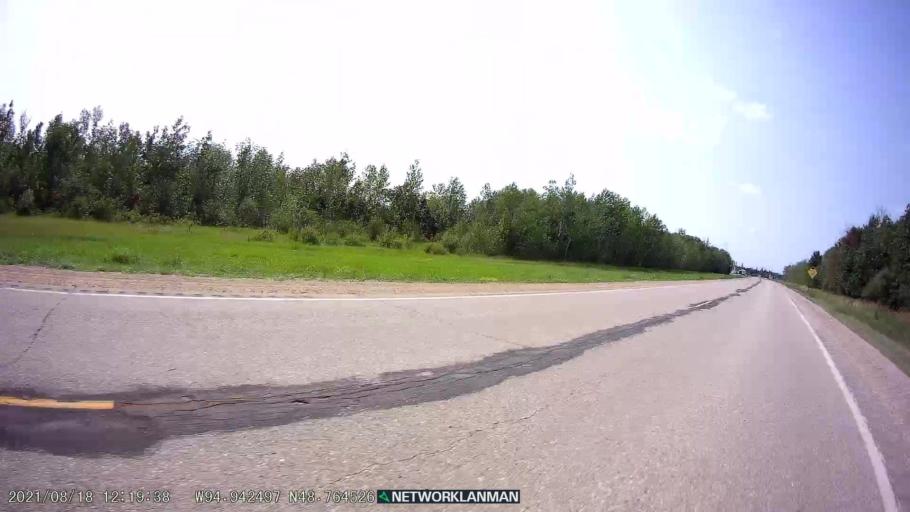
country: US
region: Minnesota
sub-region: Lake of the Woods County
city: Baudette
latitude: 48.7645
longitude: -94.9427
